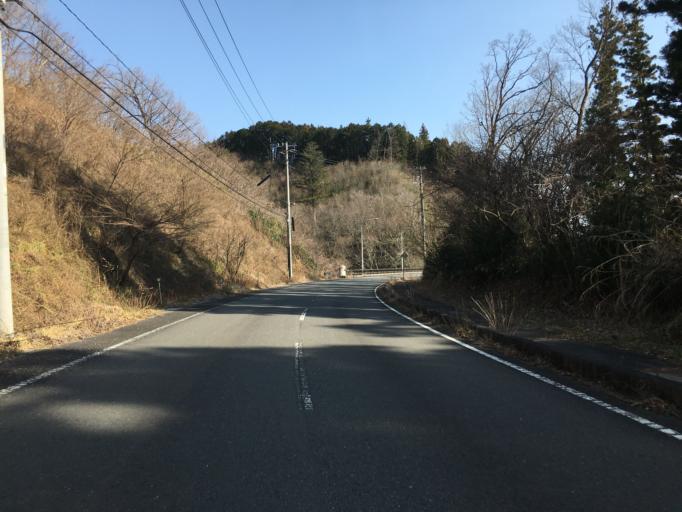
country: JP
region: Ibaraki
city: Kitaibaraki
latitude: 36.8068
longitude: 140.6336
